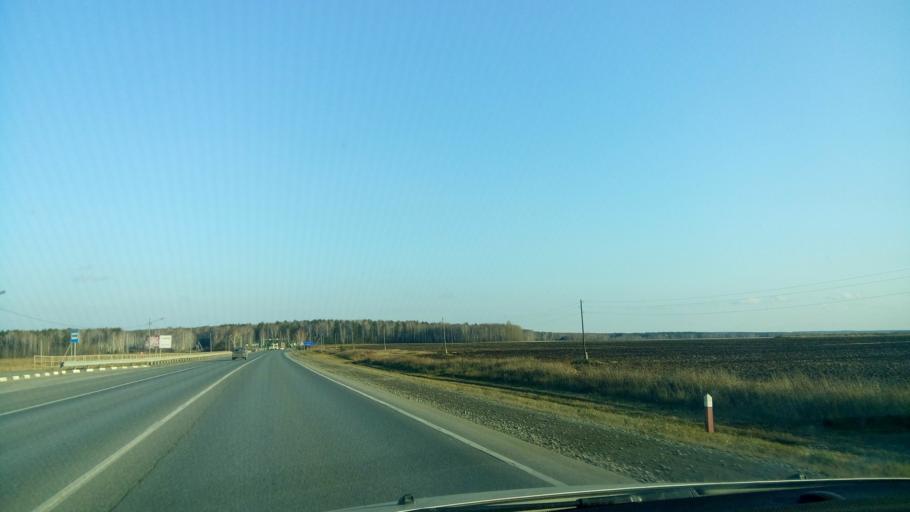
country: RU
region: Sverdlovsk
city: Verkhneye Dubrovo
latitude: 56.7414
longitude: 61.1779
